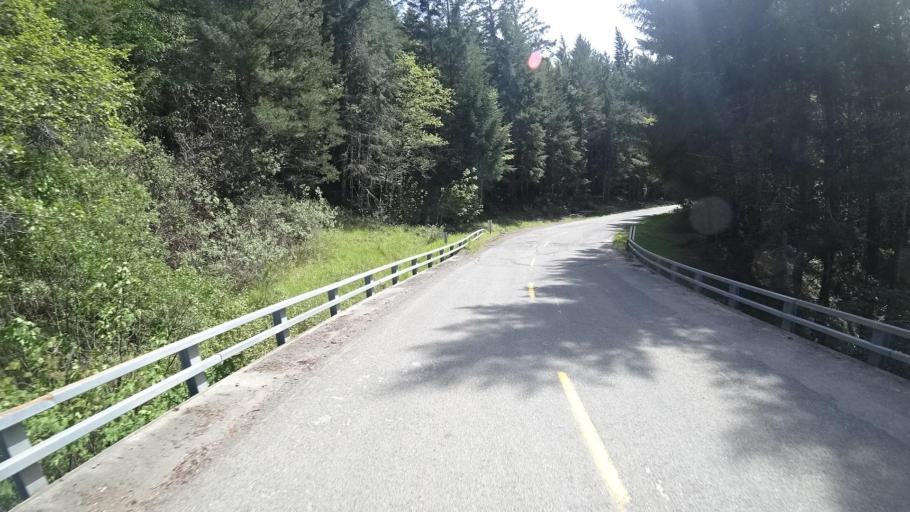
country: US
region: California
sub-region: Humboldt County
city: Redway
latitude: 40.3671
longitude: -123.7287
